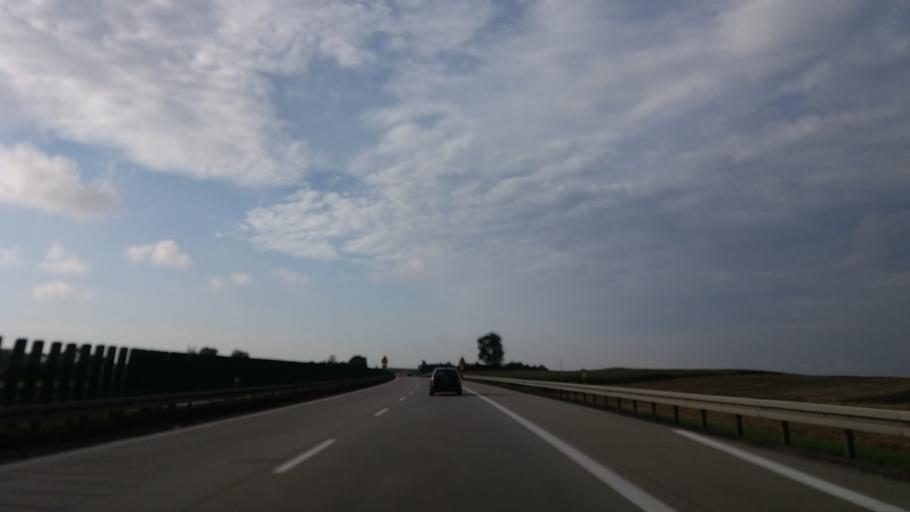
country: PL
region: Lower Silesian Voivodeship
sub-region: Powiat sredzki
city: Udanin
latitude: 51.1022
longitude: 16.4037
